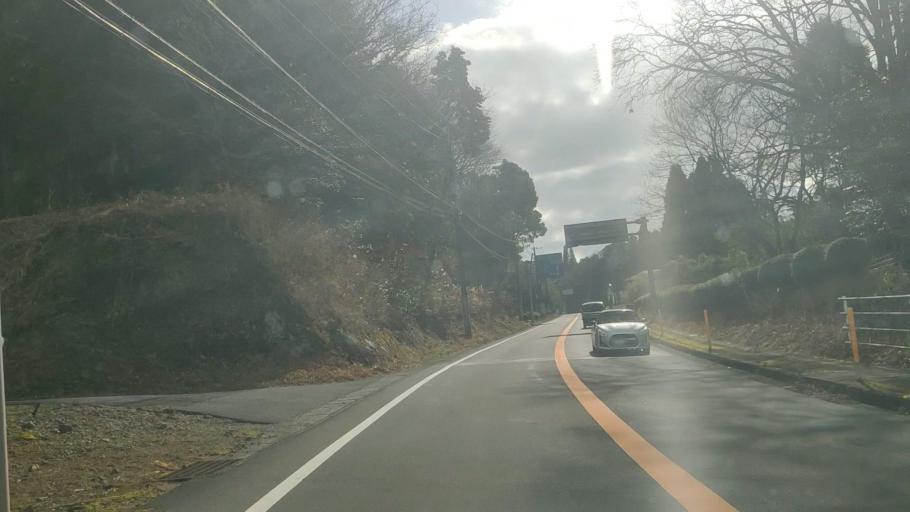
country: JP
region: Kagoshima
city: Kajiki
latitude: 31.8301
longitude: 130.6891
